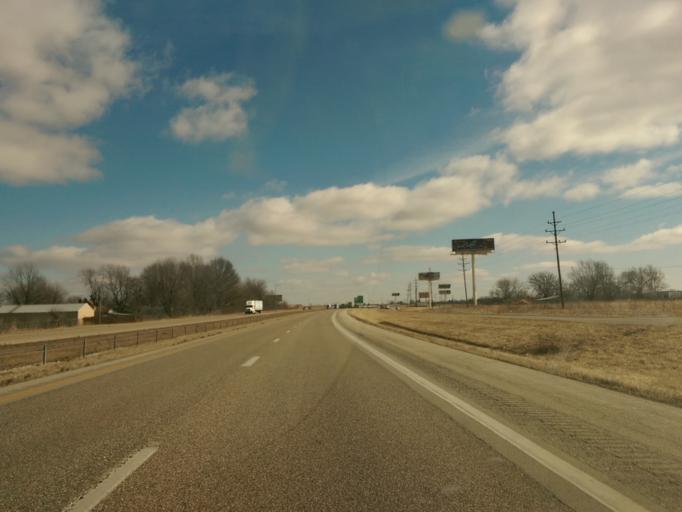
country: US
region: Missouri
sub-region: Montgomery County
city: Montgomery City
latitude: 38.8766
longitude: -91.3817
